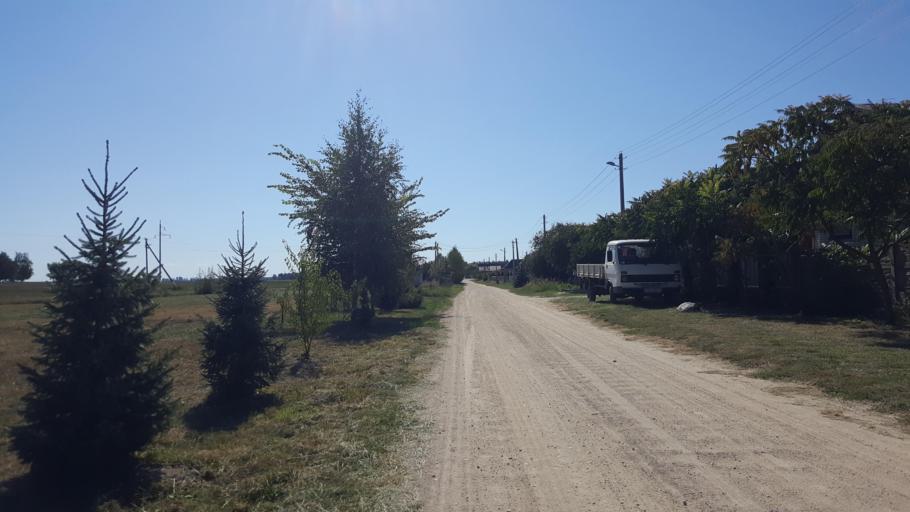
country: BY
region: Brest
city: Vysokaye
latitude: 52.2627
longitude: 23.5024
